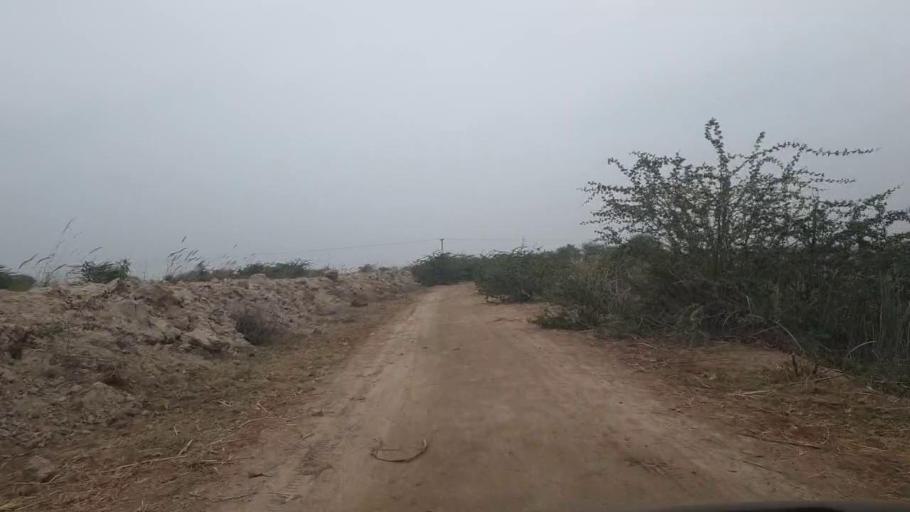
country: PK
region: Sindh
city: Tando Adam
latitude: 25.8378
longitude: 68.7232
